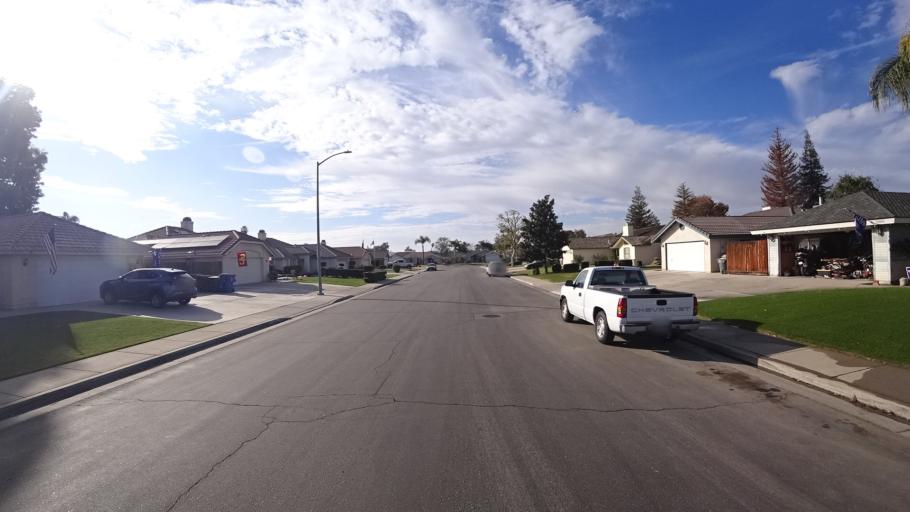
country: US
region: California
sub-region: Kern County
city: Greenacres
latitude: 35.3937
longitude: -119.1127
